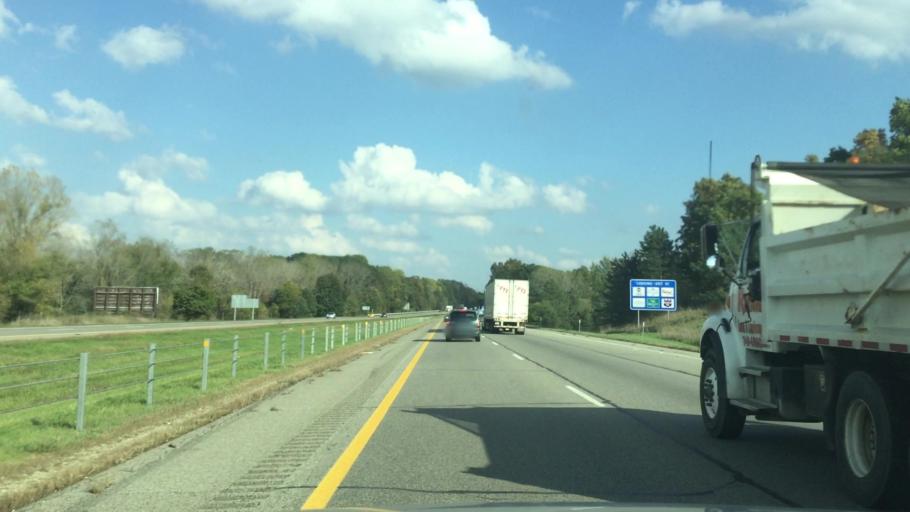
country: US
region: Michigan
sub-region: Calhoun County
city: Lakeview
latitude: 42.2650
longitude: -85.2328
